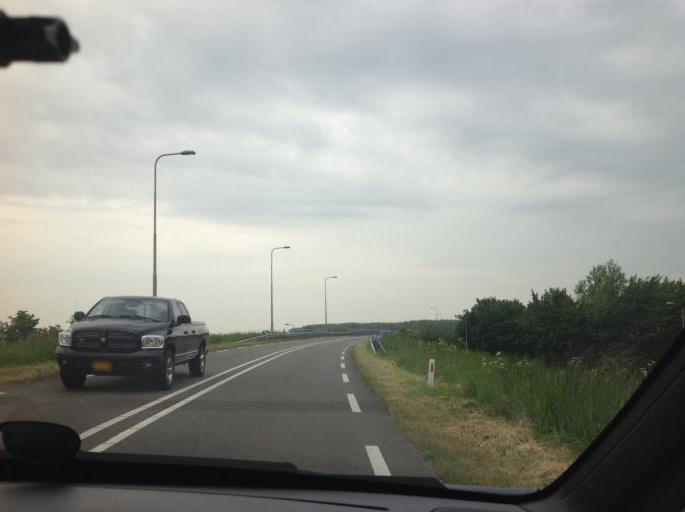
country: NL
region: Zeeland
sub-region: Gemeente Goes
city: Goes
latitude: 51.4930
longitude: 3.9249
